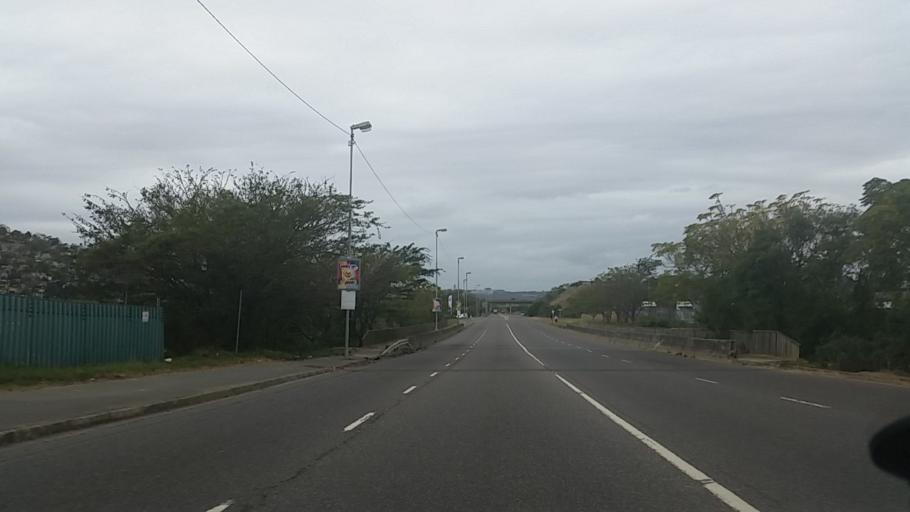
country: ZA
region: KwaZulu-Natal
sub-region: eThekwini Metropolitan Municipality
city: Berea
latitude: -29.8569
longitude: 30.9365
